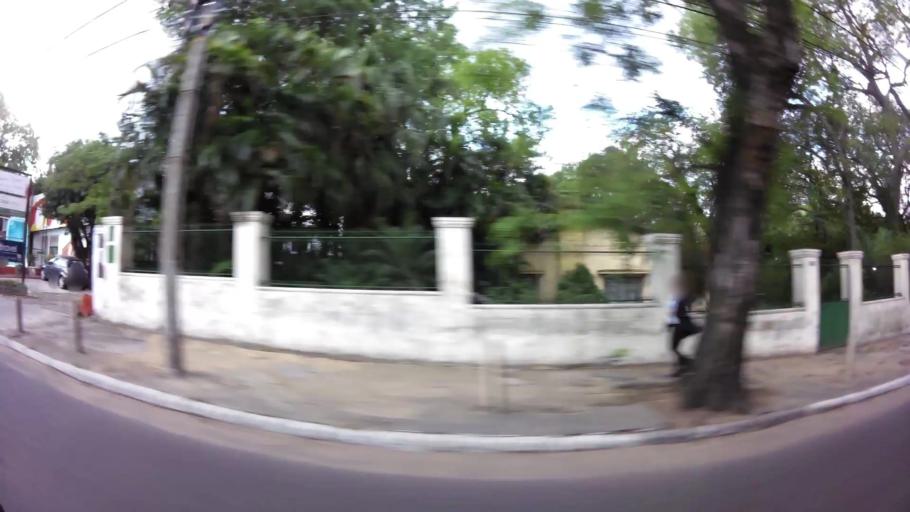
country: PY
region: Asuncion
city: Asuncion
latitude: -25.2906
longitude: -57.5934
